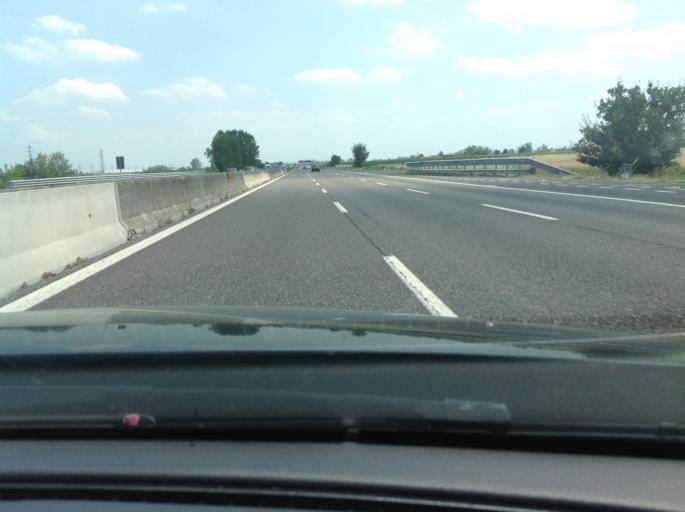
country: IT
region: Emilia-Romagna
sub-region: Provincia di Piacenza
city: Roveleto
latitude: 44.9753
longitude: 9.8756
